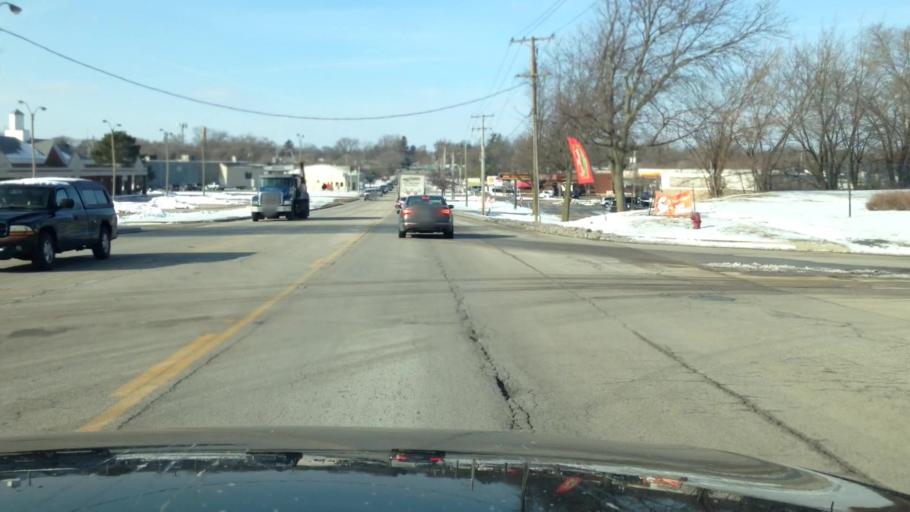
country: US
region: Illinois
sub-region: McHenry County
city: Woodstock
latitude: 42.3143
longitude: -88.4360
